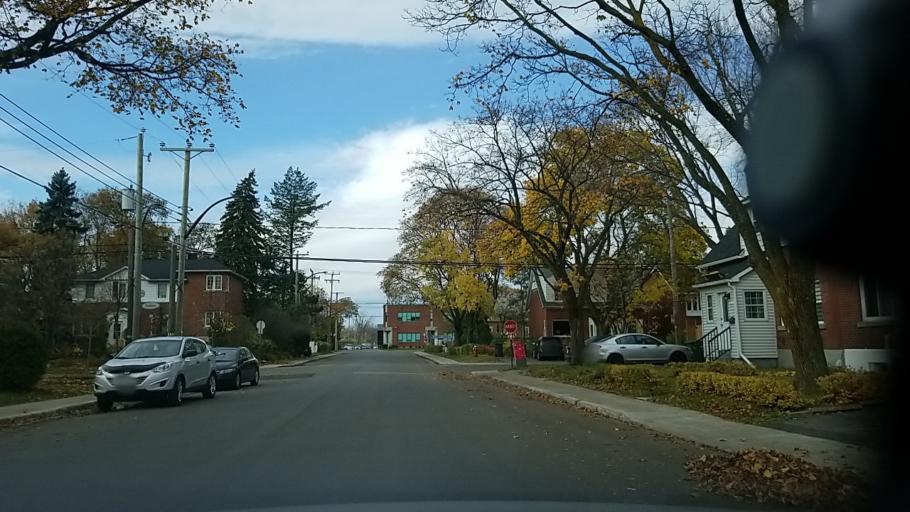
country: CA
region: Quebec
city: Saint-Laurent
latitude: 45.5132
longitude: -73.6633
